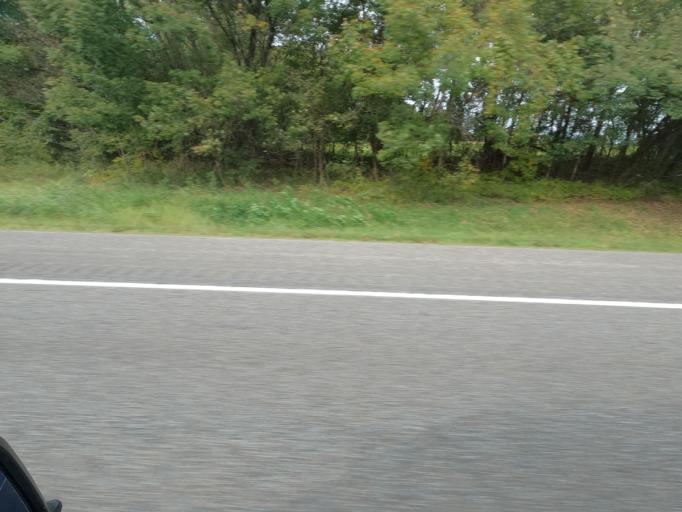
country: US
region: Tennessee
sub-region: Haywood County
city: Brownsville
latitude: 35.5626
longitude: -89.1703
